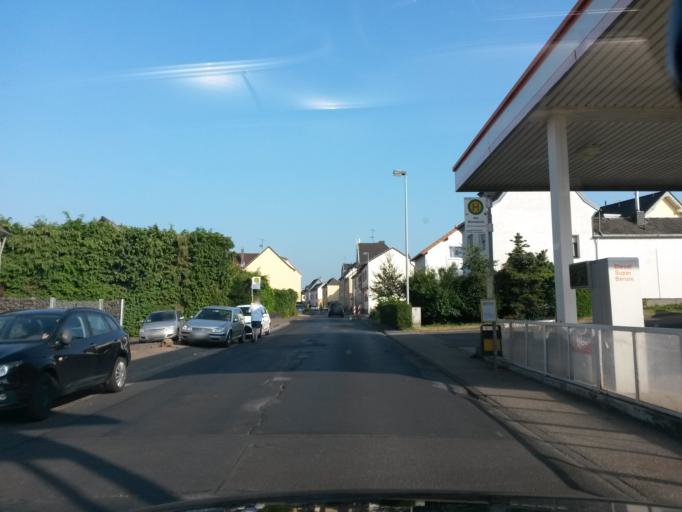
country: DE
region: North Rhine-Westphalia
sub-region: Regierungsbezirk Koln
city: Alfter
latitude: 50.7284
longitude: 7.0207
